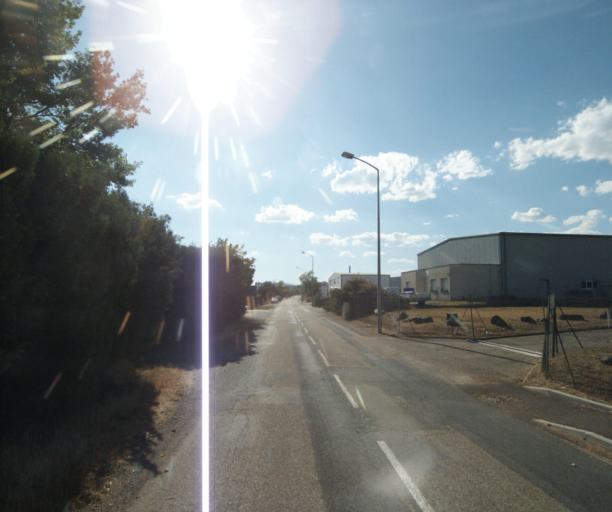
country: FR
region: Rhone-Alpes
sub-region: Departement du Rhone
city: Lentilly
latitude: 45.8168
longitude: 4.6857
